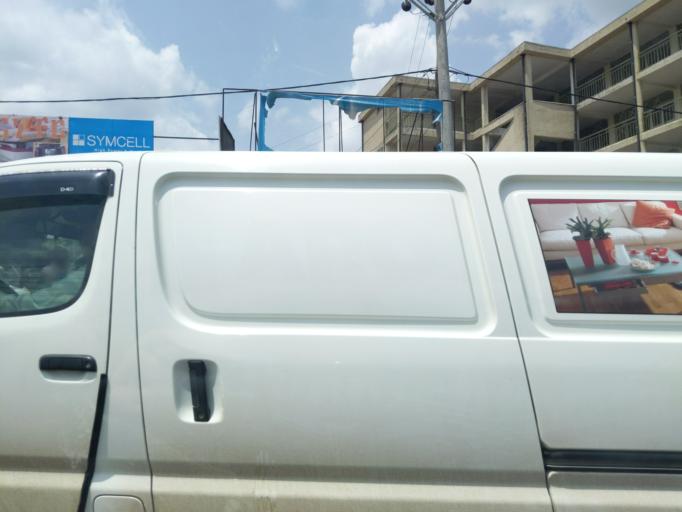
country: ET
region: Adis Abeba
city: Addis Ababa
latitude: 8.9543
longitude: 38.7637
